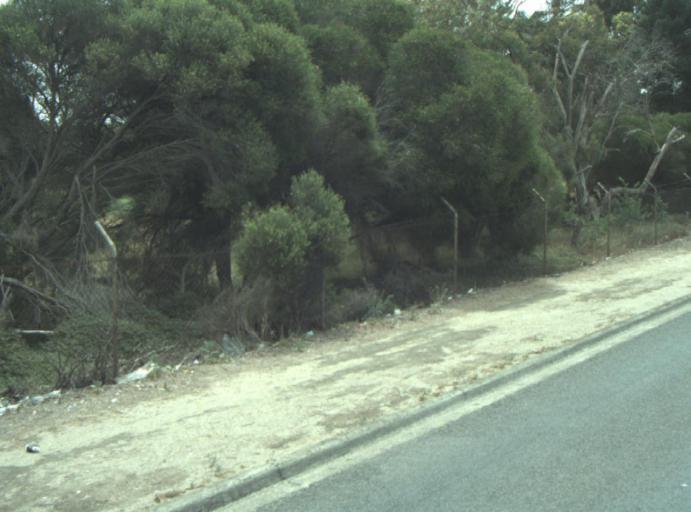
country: AU
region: Victoria
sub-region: Greater Geelong
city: Hamlyn Heights
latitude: -38.1234
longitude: 144.3409
